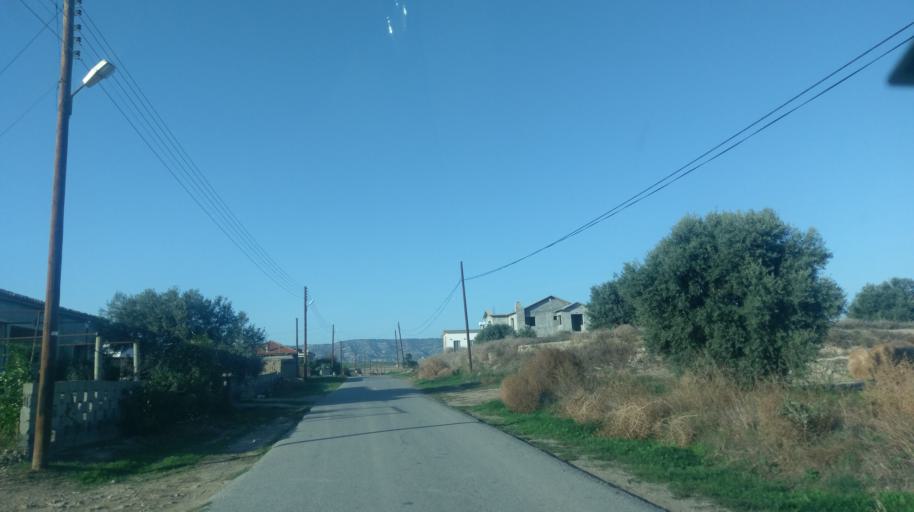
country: CY
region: Ammochostos
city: Lefkonoiko
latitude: 35.2698
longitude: 33.6584
